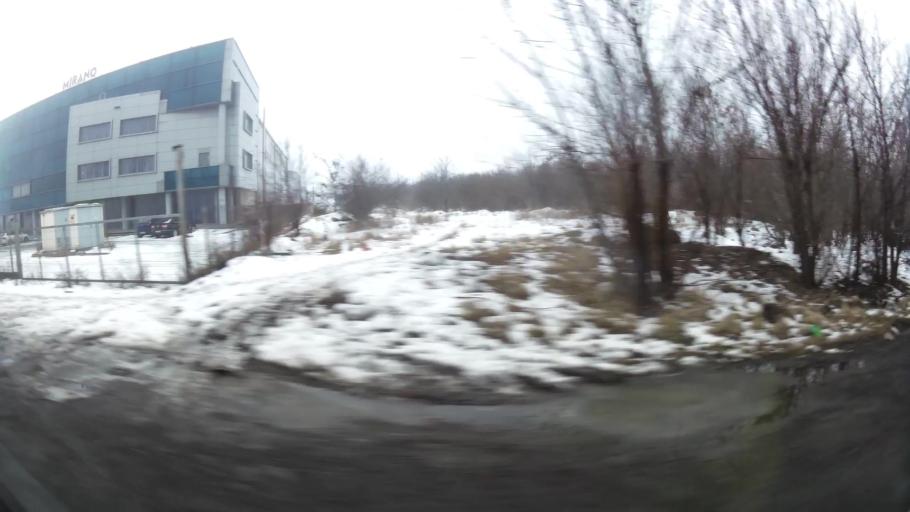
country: RO
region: Ilfov
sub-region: Comuna Chiajna
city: Chiajna
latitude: 44.4316
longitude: 25.9673
